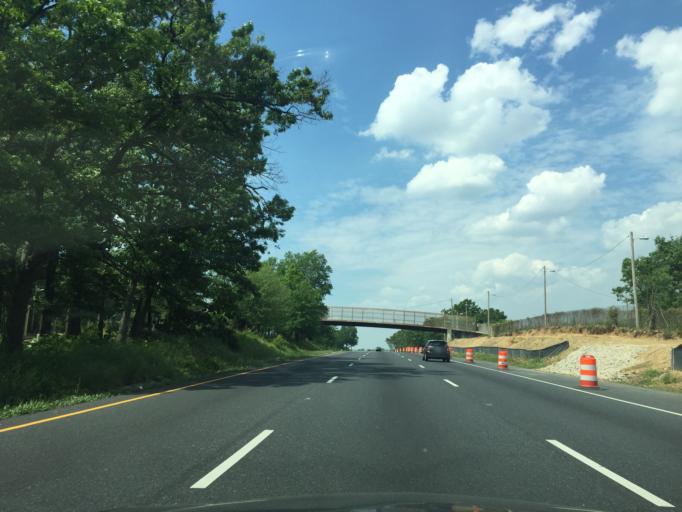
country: US
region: Maryland
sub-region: Baltimore County
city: Baltimore Highlands
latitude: 39.2374
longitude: -76.6489
